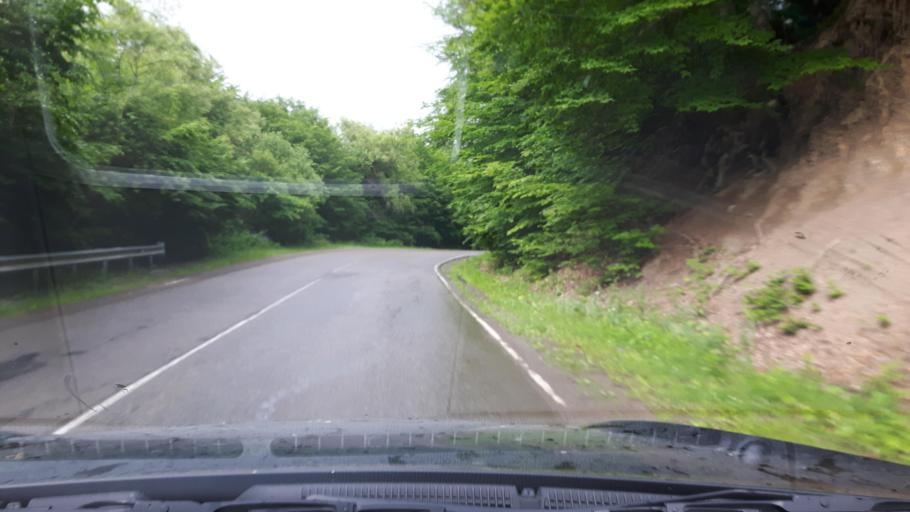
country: GE
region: Kakheti
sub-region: Telavi
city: Telavi
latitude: 41.8837
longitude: 45.3599
